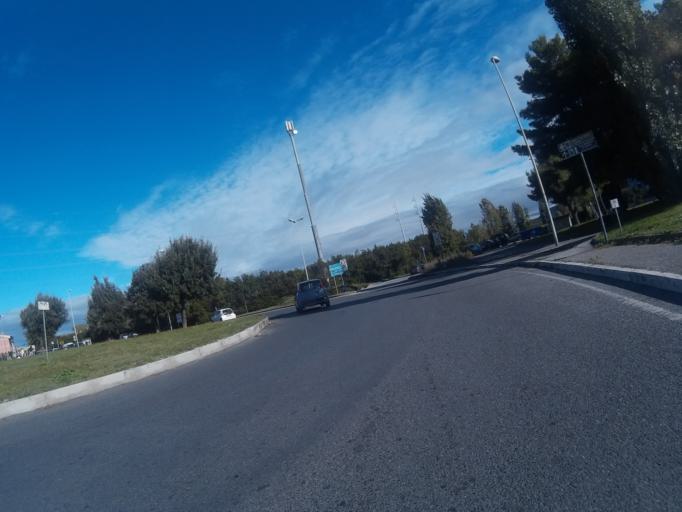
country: IT
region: Tuscany
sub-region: Provincia di Livorno
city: Livorno
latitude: 43.5312
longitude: 10.3424
